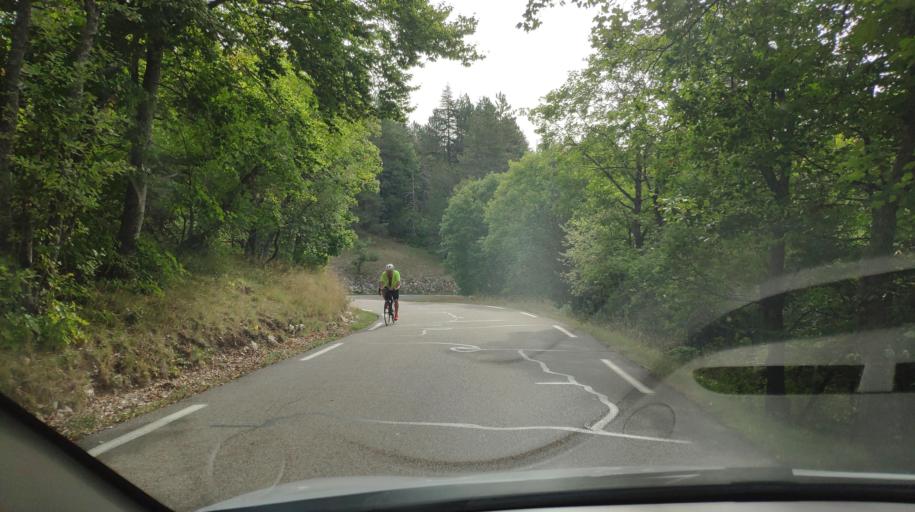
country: FR
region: Provence-Alpes-Cote d'Azur
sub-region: Departement du Vaucluse
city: Sault
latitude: 44.1522
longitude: 5.3536
